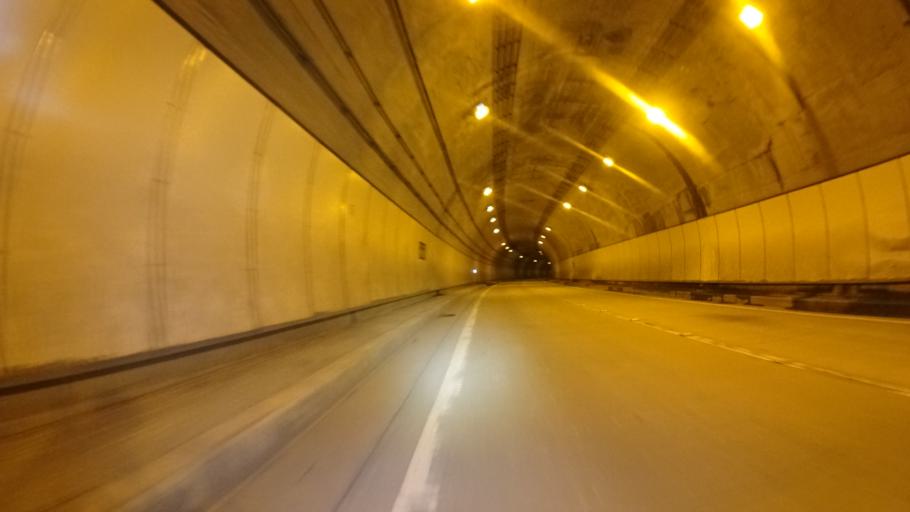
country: JP
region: Yamanashi
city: Uenohara
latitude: 35.6959
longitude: 139.1036
